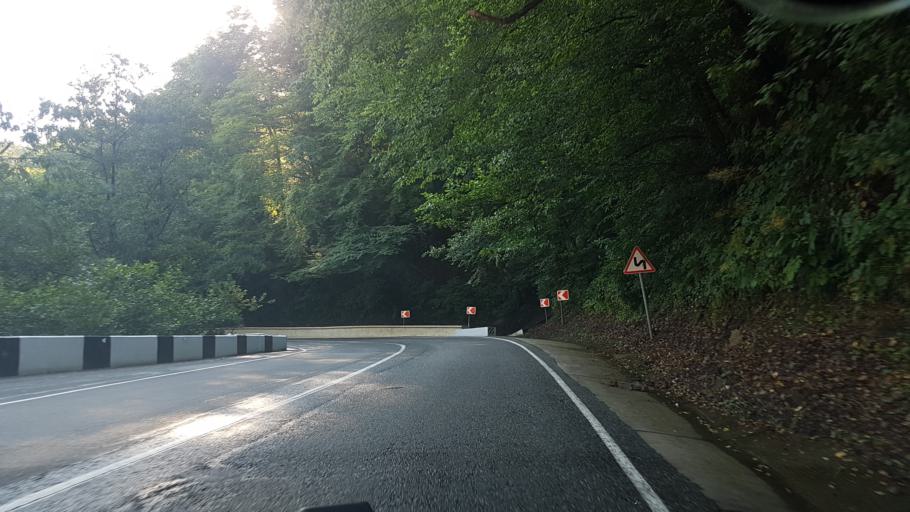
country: RU
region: Krasnodarskiy
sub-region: Sochi City
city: Lazarevskoye
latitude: 43.8740
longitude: 39.3984
